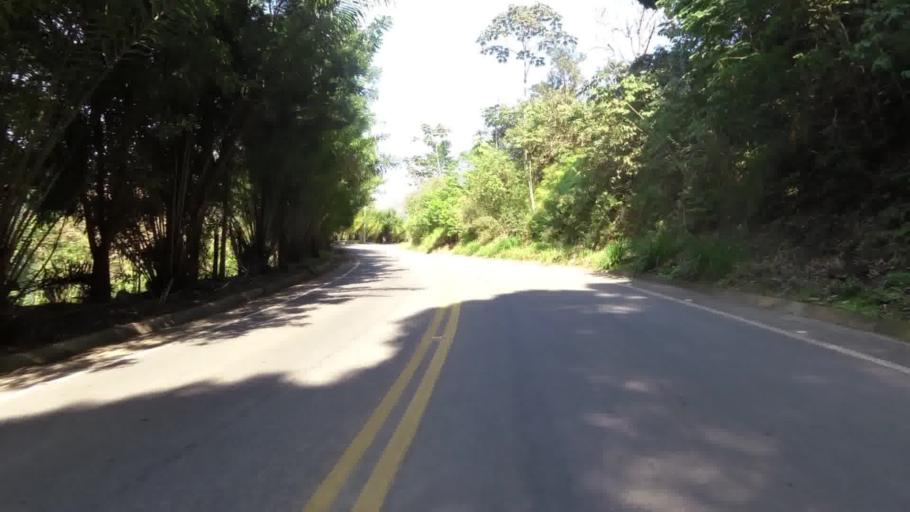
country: BR
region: Espirito Santo
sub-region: Alfredo Chaves
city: Alfredo Chaves
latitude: -20.6140
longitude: -40.7786
